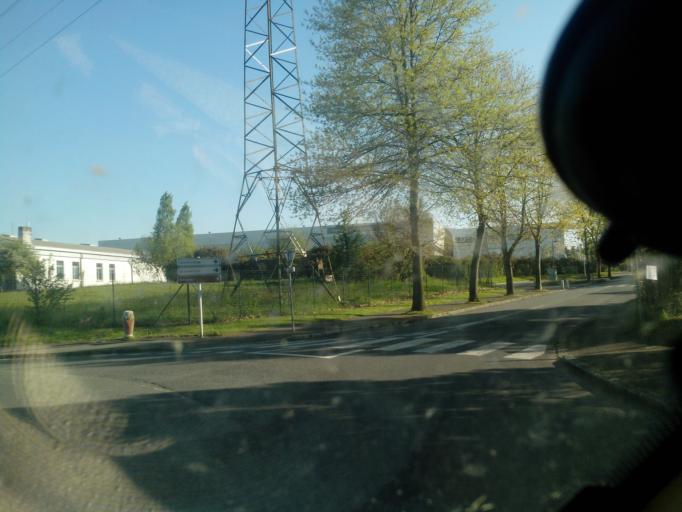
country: FR
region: Pays de la Loire
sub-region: Departement de la Loire-Atlantique
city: Orvault
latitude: 47.2525
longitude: -1.6122
